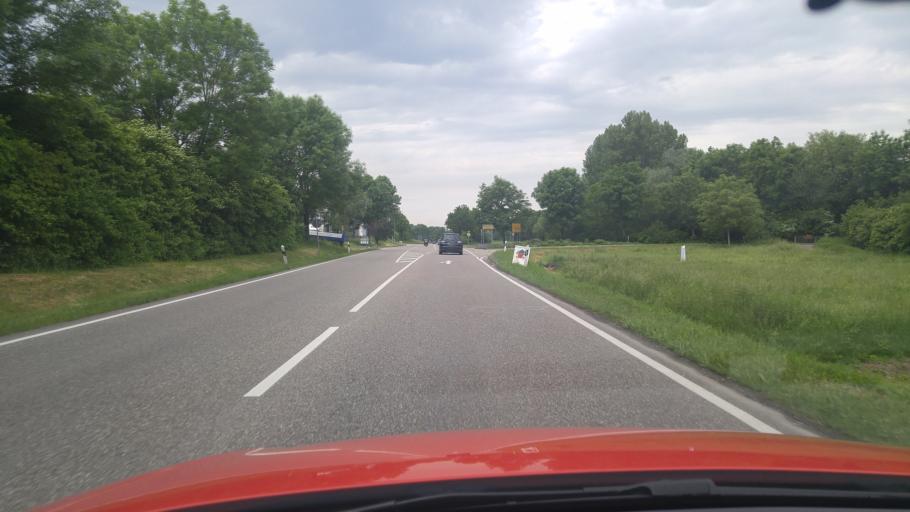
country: DE
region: Baden-Wuerttemberg
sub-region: Regierungsbezirk Stuttgart
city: Ellhofen
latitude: 49.1450
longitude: 9.3372
